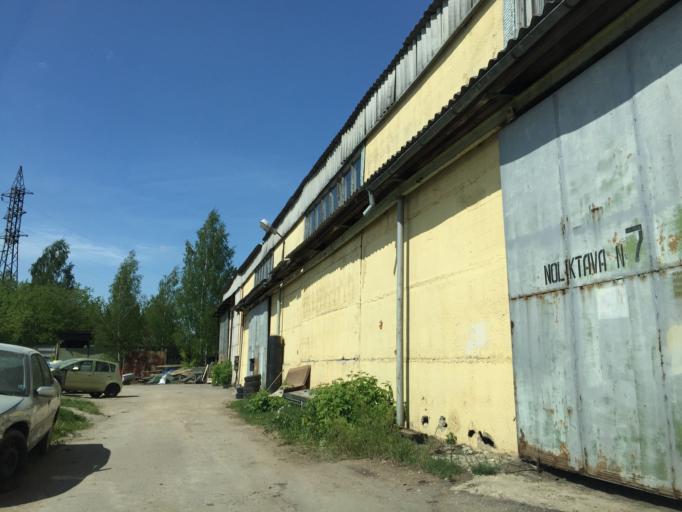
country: LV
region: Riga
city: Bergi
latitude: 57.0000
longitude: 24.2690
